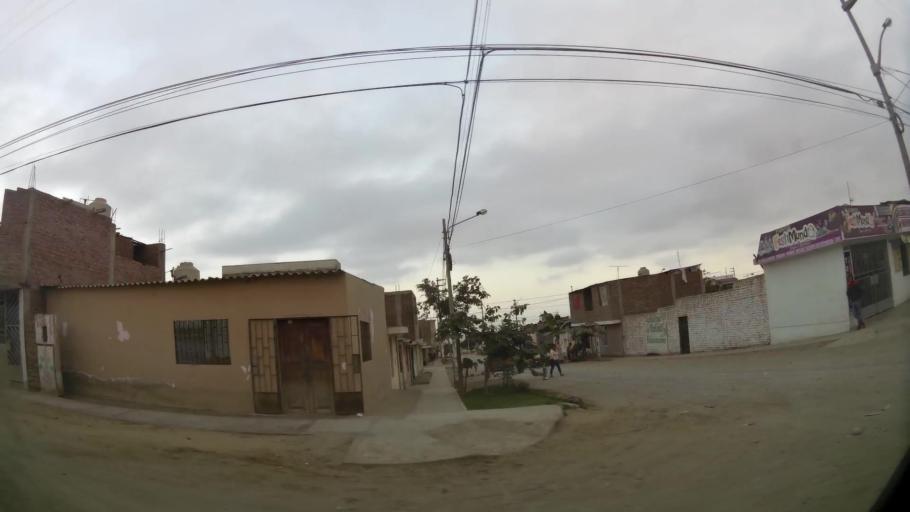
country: PE
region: La Libertad
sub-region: Provincia de Trujillo
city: El Porvenir
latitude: -8.0669
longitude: -79.0192
